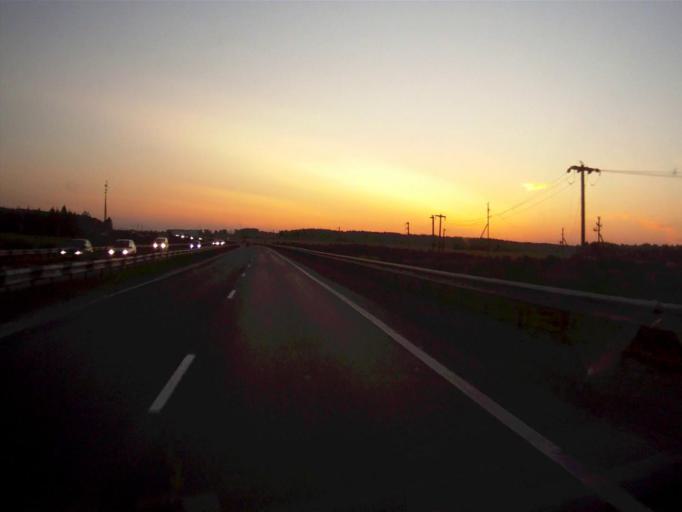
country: RU
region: Chelyabinsk
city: Roshchino
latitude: 55.1947
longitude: 61.2063
